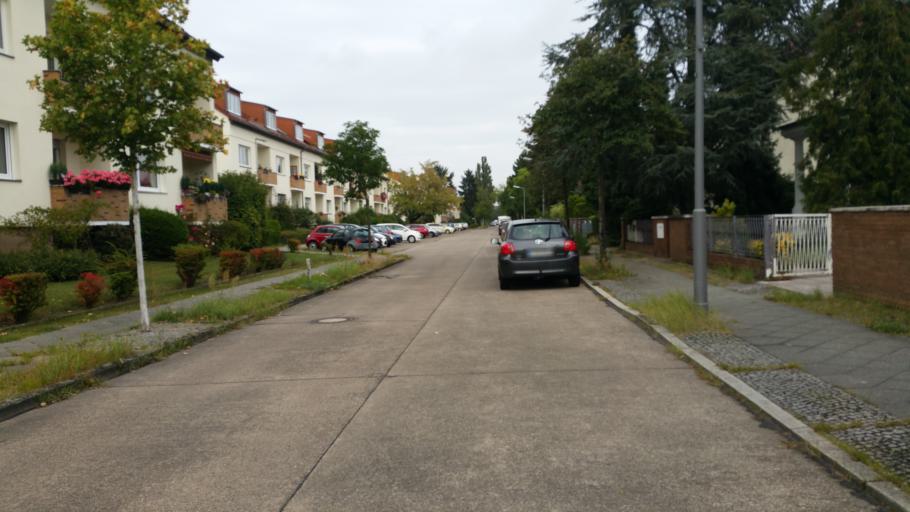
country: DE
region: Berlin
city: Wilhelmstadt
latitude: 52.5126
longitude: 13.1713
